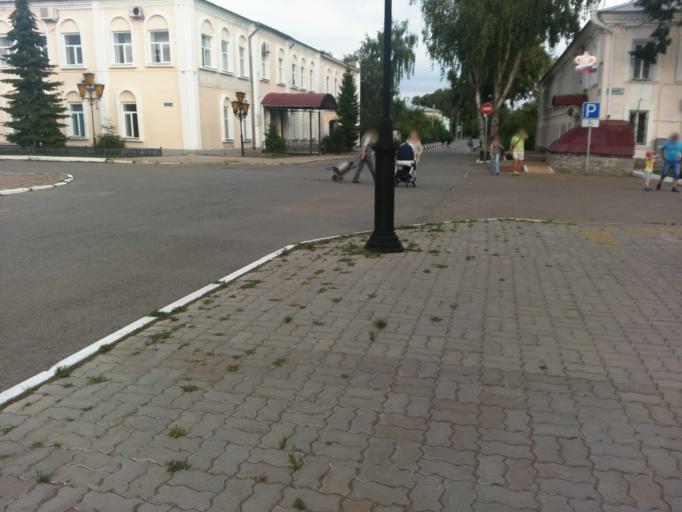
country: RU
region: Tatarstan
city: Yelabuga
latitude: 55.7557
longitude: 52.0615
